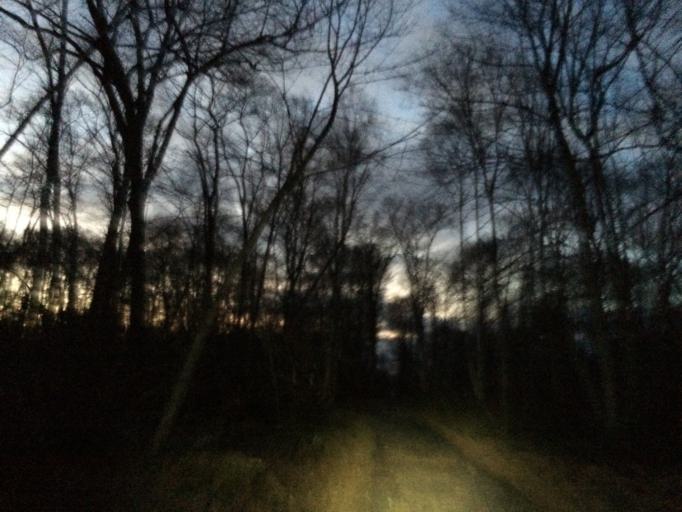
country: FR
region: Picardie
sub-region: Departement de l'Oise
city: Coye-la-Foret
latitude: 49.1521
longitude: 2.4816
